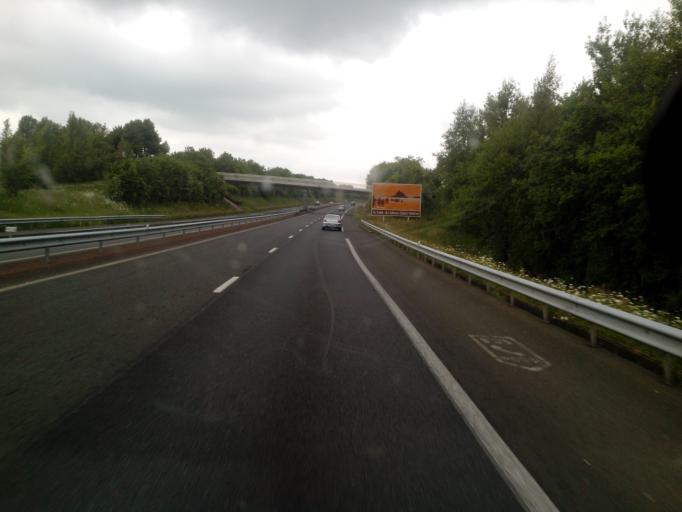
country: FR
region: Lower Normandy
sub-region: Departement de la Manche
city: Saint-James
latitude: 48.5504
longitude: -1.3416
